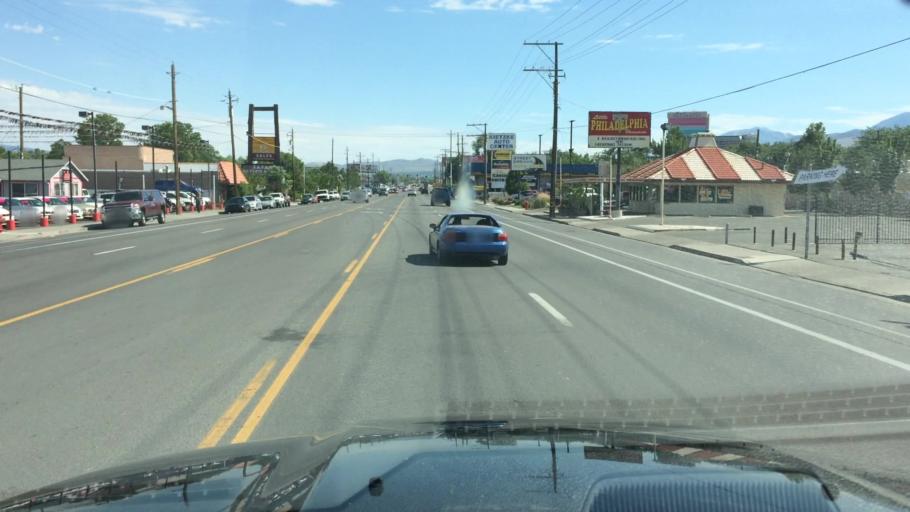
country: US
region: Nevada
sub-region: Washoe County
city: Reno
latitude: 39.4988
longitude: -119.7891
